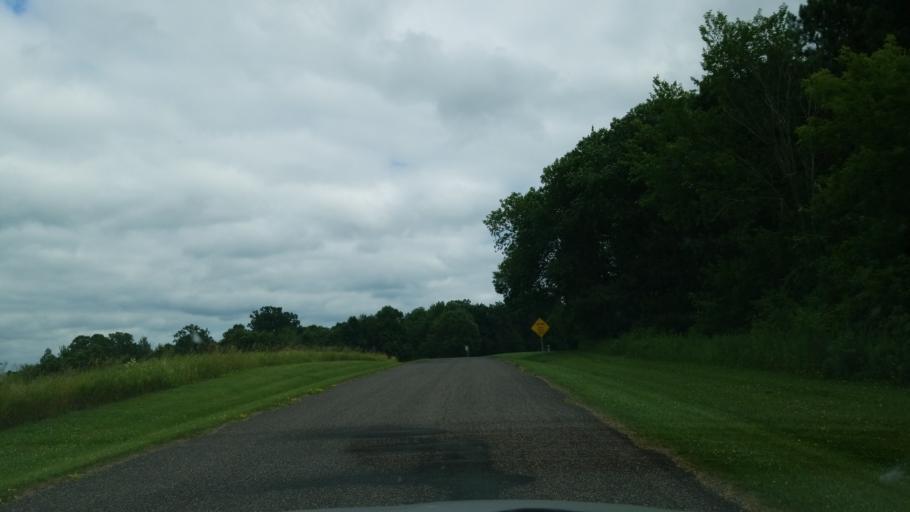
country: US
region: Wisconsin
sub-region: Saint Croix County
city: Glenwood City
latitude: 45.0112
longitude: -92.1644
